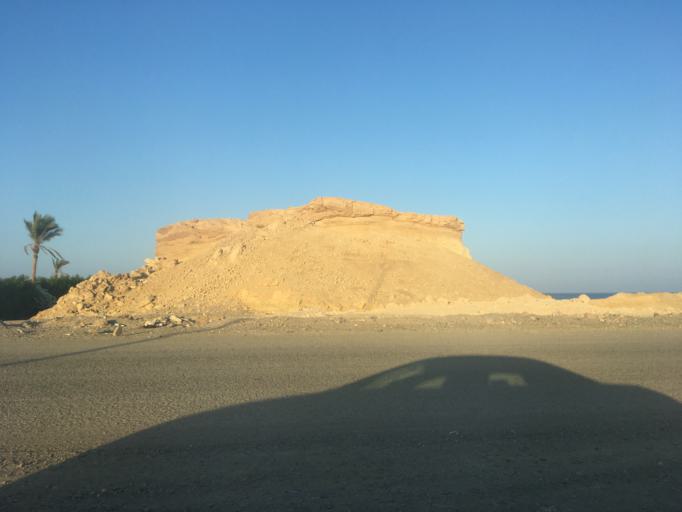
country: EG
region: Red Sea
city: Marsa Alam
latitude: 25.0842
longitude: 34.8802
